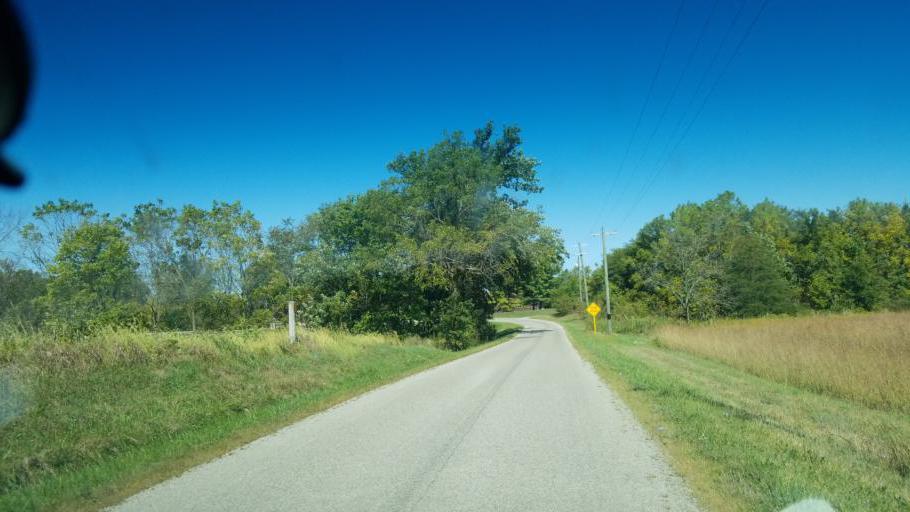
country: US
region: Ohio
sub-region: Union County
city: Richwood
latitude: 40.4778
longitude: -83.4068
